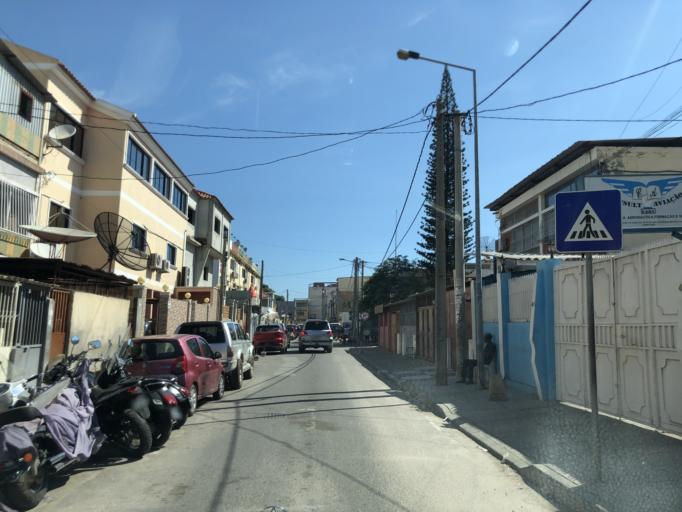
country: AO
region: Luanda
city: Luanda
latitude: -8.8464
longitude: 13.2289
